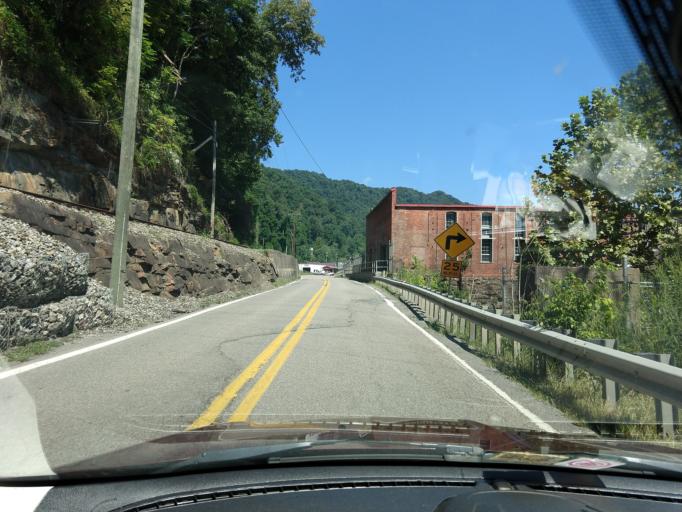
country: US
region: West Virginia
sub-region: Fayette County
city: Ansted
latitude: 38.1475
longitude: -81.2145
